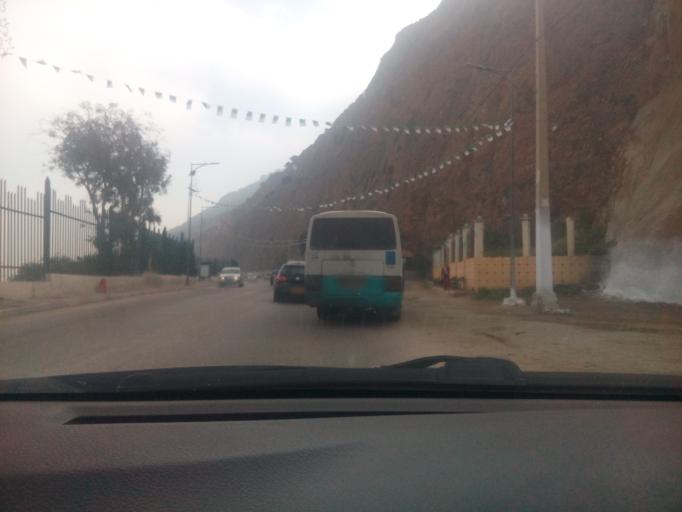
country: DZ
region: Oran
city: Mers el Kebir
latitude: 35.7122
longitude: -0.6835
